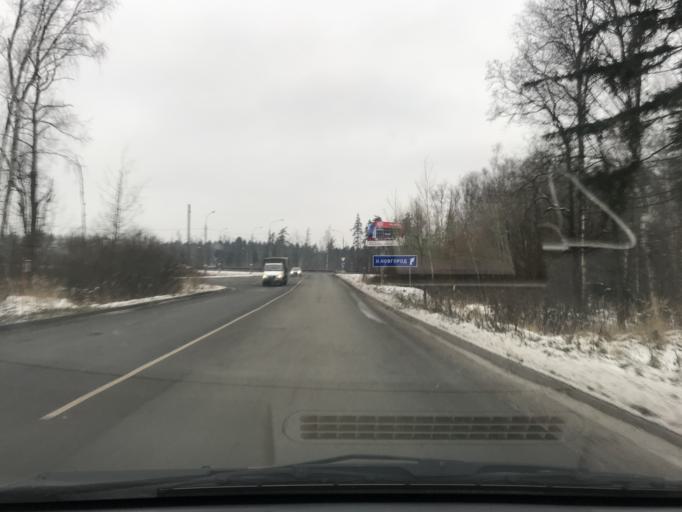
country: RU
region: Moskovskaya
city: Noginsk
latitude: 55.8294
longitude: 38.4508
